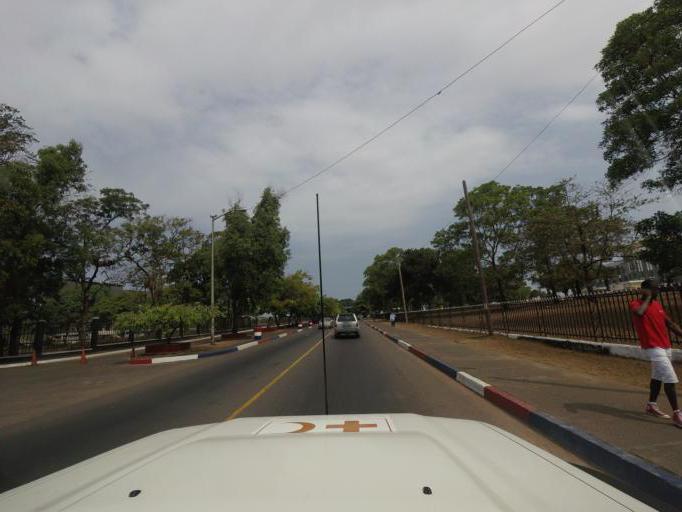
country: LR
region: Montserrado
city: Monrovia
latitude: 6.3000
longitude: -10.7962
